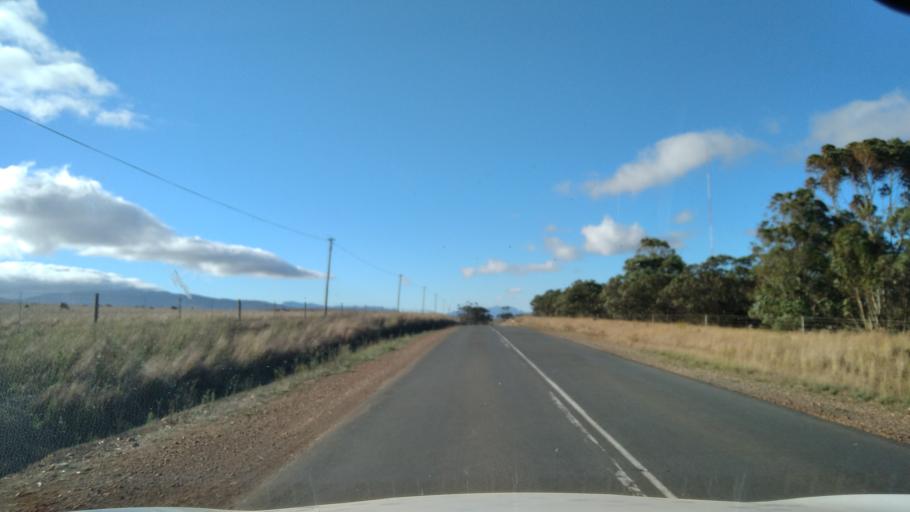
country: ZA
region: Western Cape
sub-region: Overberg District Municipality
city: Caledon
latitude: -34.2172
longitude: 19.2763
